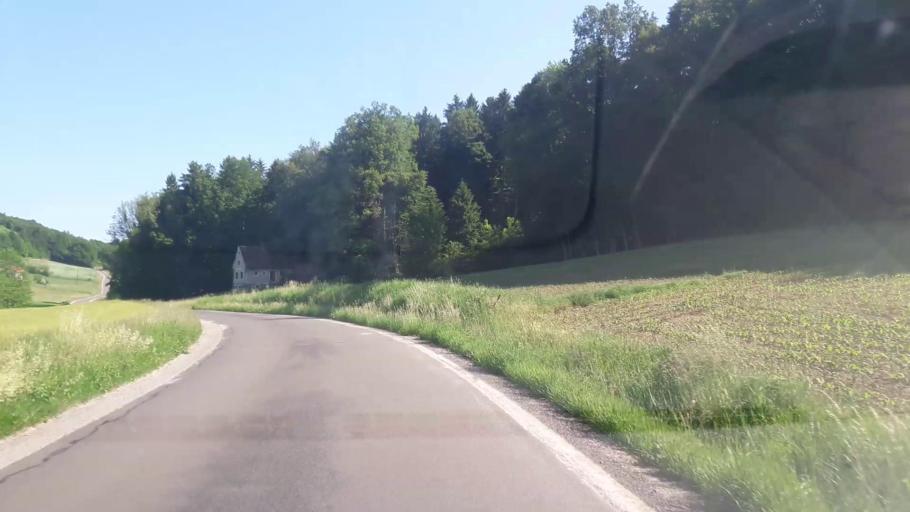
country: AT
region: Styria
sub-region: Politischer Bezirk Hartberg-Fuerstenfeld
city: UEbersbach
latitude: 46.9944
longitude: 16.0450
